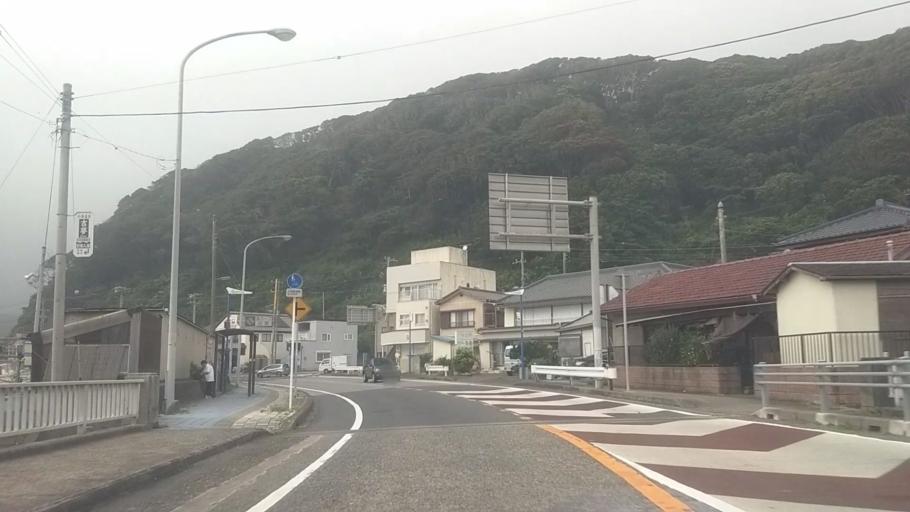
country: JP
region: Chiba
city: Kawaguchi
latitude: 35.1225
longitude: 140.1984
